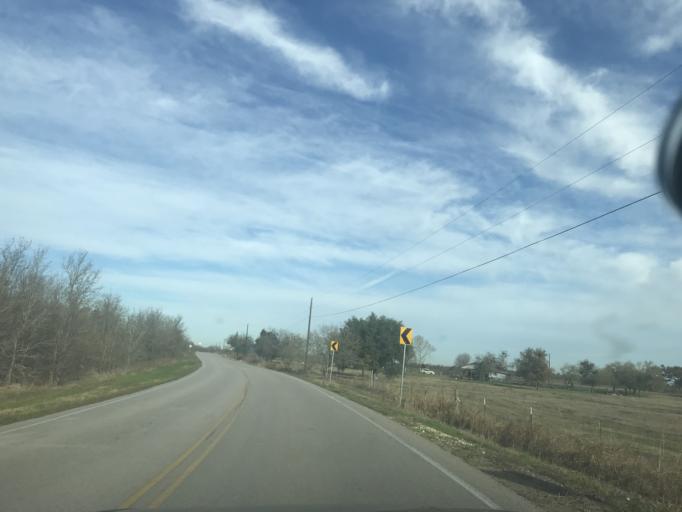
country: US
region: Texas
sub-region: Travis County
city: Manor
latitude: 30.2926
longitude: -97.5231
